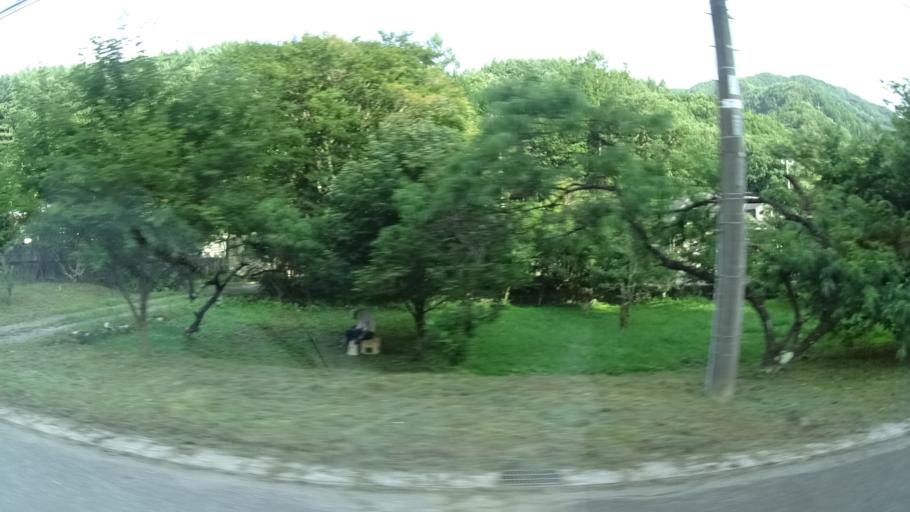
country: JP
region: Tochigi
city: Nikko
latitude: 36.6552
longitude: 139.4552
